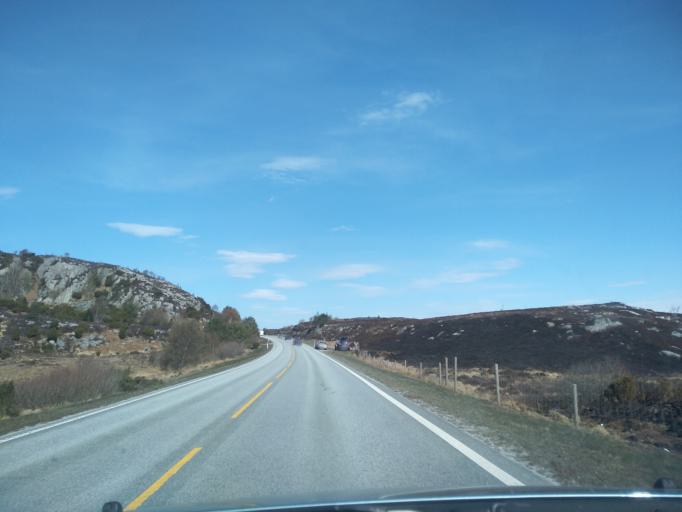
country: NO
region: Rogaland
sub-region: Bokn
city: Bokn
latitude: 59.1966
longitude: 5.4584
